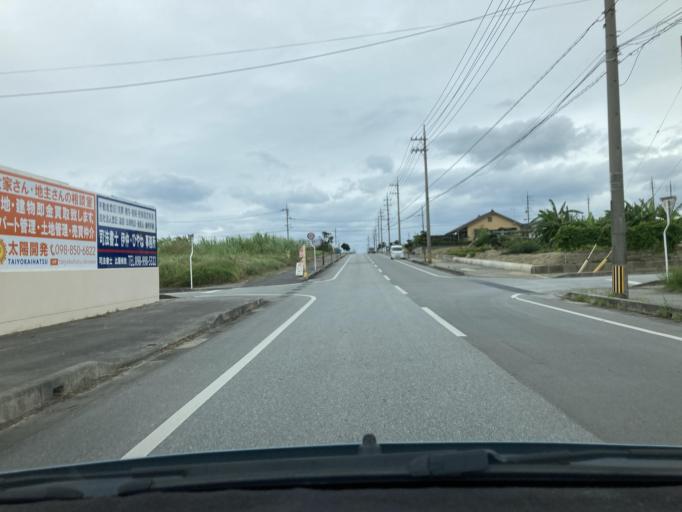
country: JP
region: Okinawa
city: Tomigusuku
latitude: 26.1608
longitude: 127.7056
